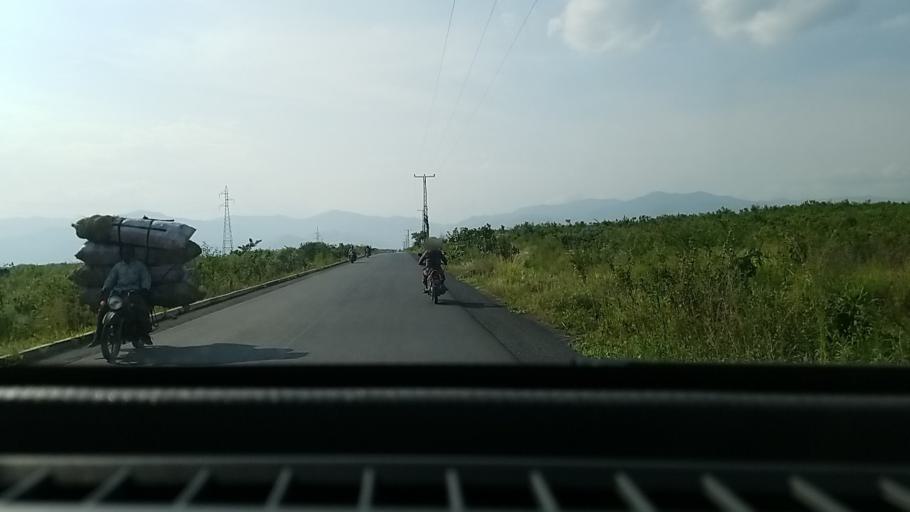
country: CD
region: Nord Kivu
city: Sake
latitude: -1.5978
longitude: 29.1095
